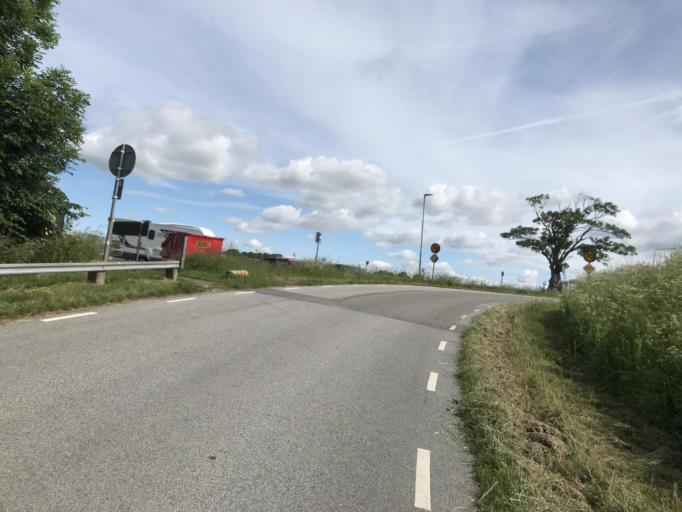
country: SE
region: Skane
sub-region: Helsingborg
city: Rydeback
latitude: 55.9434
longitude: 12.7715
